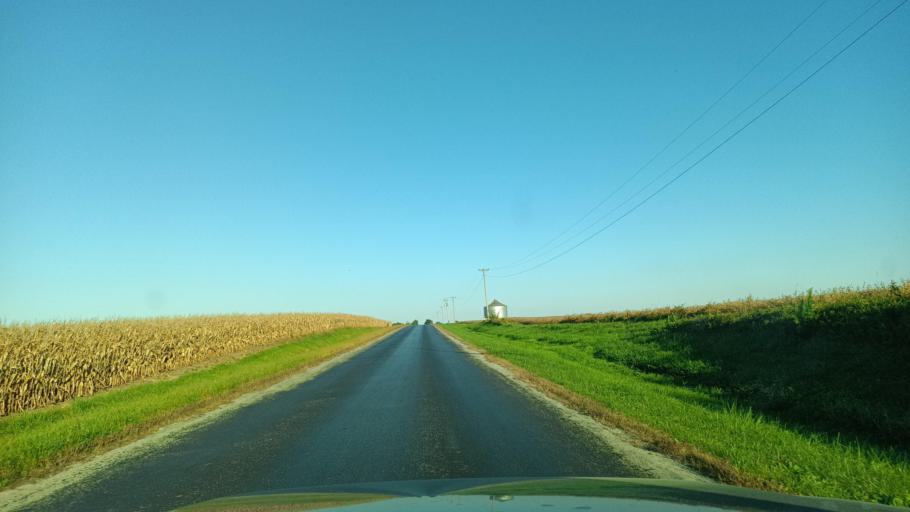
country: US
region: Illinois
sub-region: Warren County
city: Monmouth
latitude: 40.9860
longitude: -90.6236
